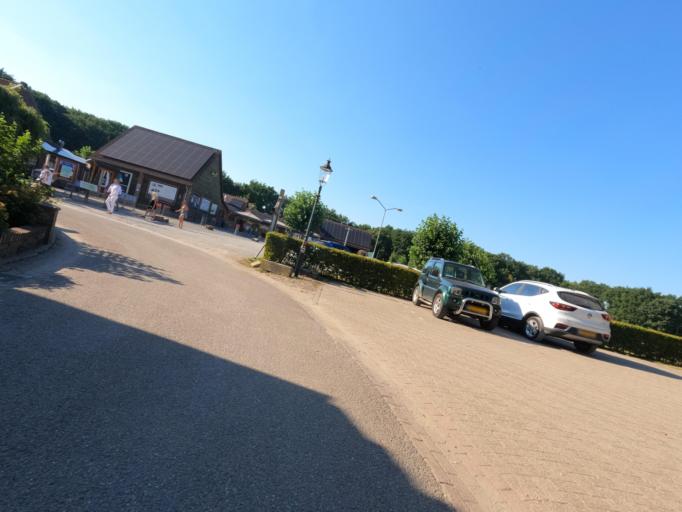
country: NL
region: Limburg
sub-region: Gemeente Roerdalen
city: Vlodrop
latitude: 51.1378
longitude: 6.1087
